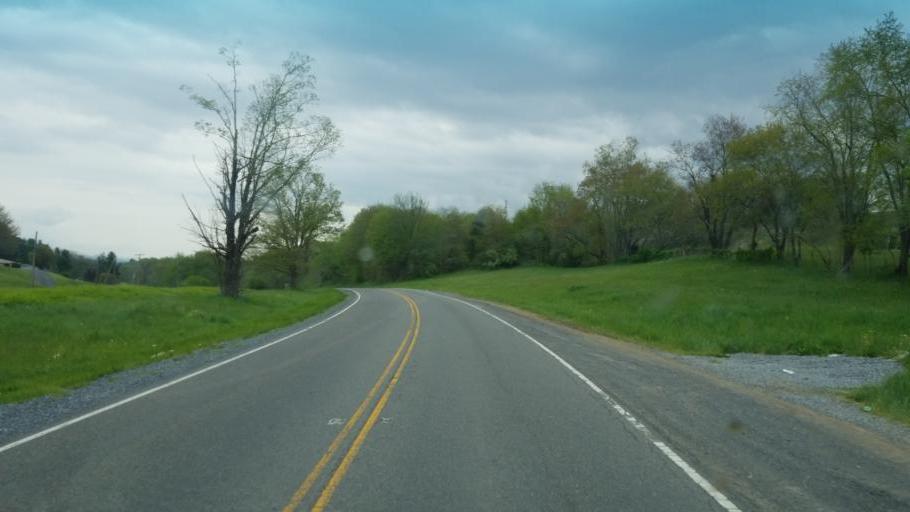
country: US
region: Virginia
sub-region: Smyth County
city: Adwolf
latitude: 36.8119
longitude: -81.5714
